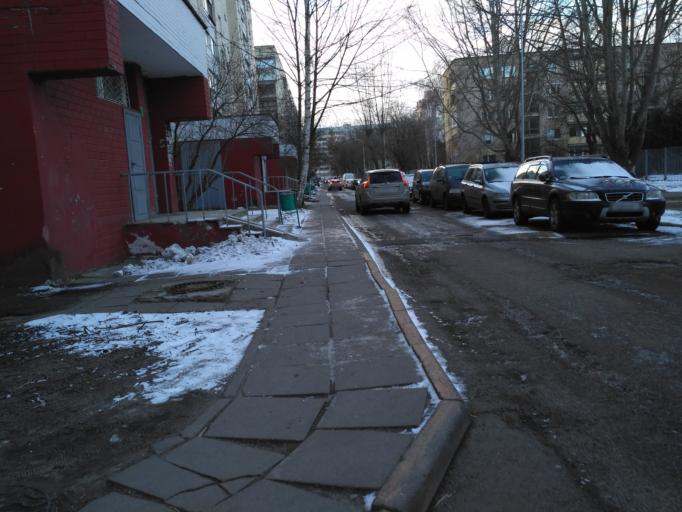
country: BY
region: Minsk
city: Minsk
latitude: 53.9208
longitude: 27.5742
